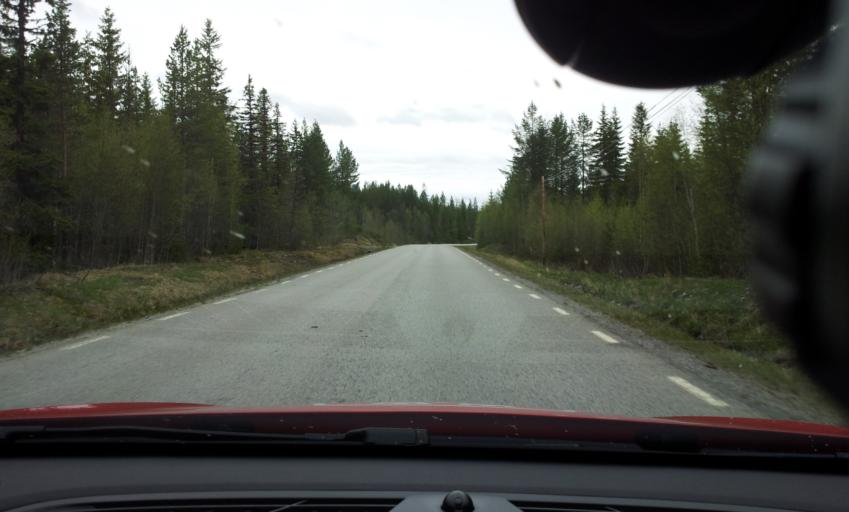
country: SE
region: Jaemtland
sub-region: Bergs Kommun
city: Hoverberg
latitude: 62.7537
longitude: 14.5682
